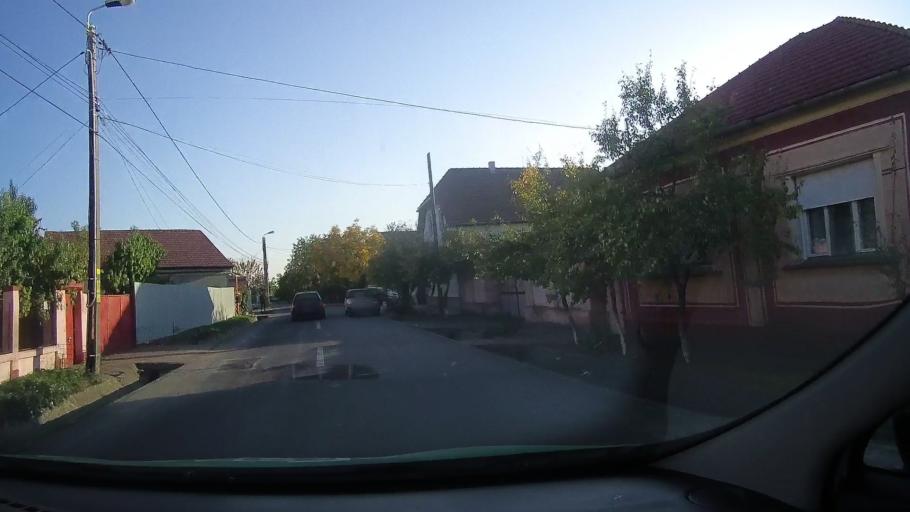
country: RO
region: Bihor
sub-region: Comuna Biharea
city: Oradea
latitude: 47.1014
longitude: 21.8963
